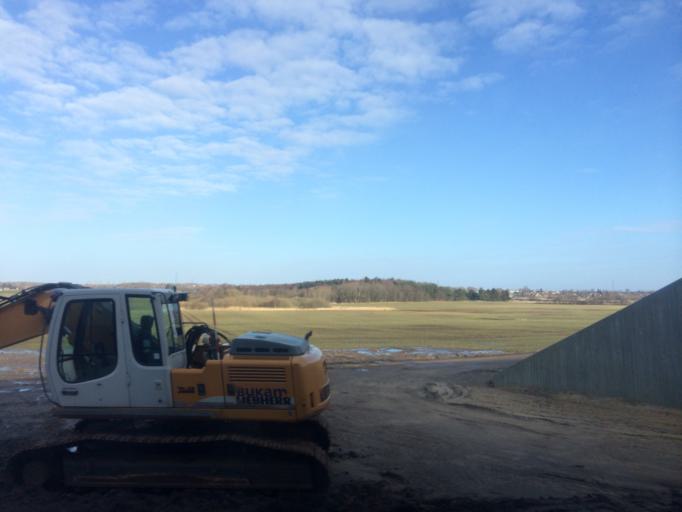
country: DK
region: Central Jutland
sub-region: Herning Kommune
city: Snejbjerg
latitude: 56.1503
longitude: 8.9057
